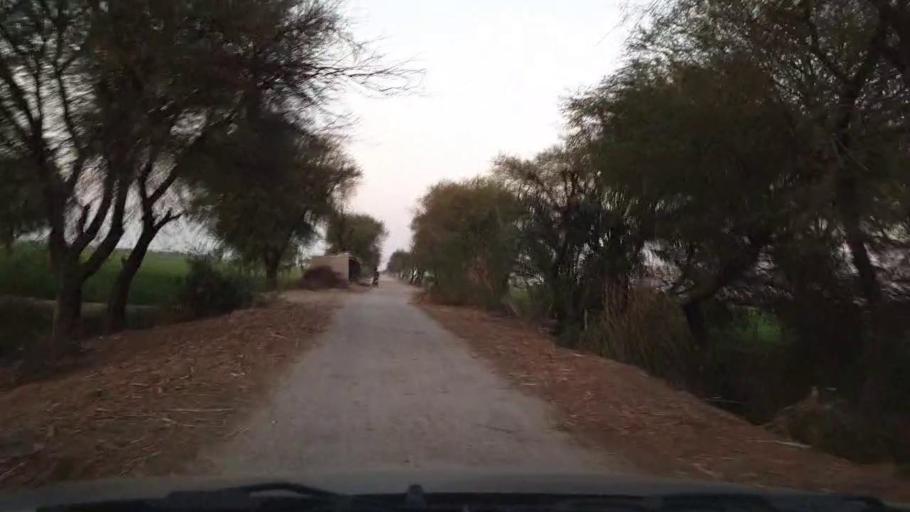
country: PK
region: Sindh
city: Jhol
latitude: 25.9409
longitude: 68.9725
